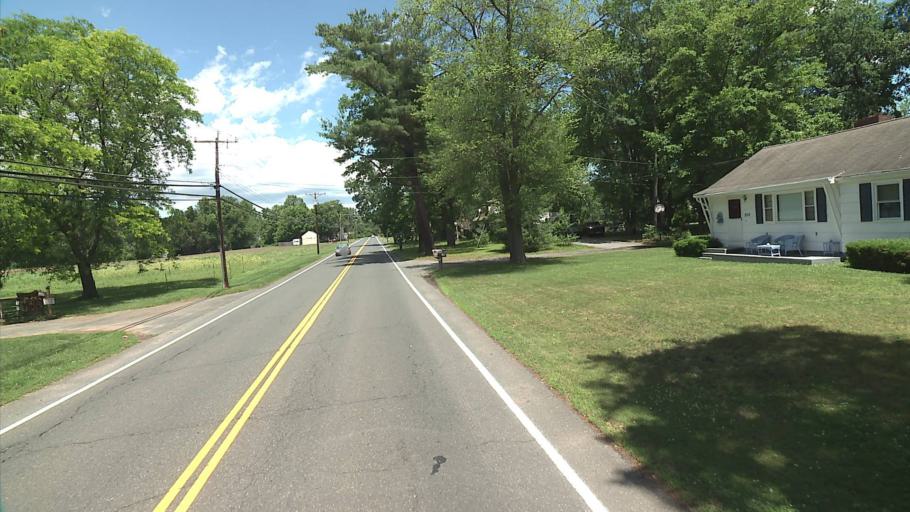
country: US
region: Connecticut
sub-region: Hartford County
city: Sherwood Manor
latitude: 42.0173
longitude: -72.5408
